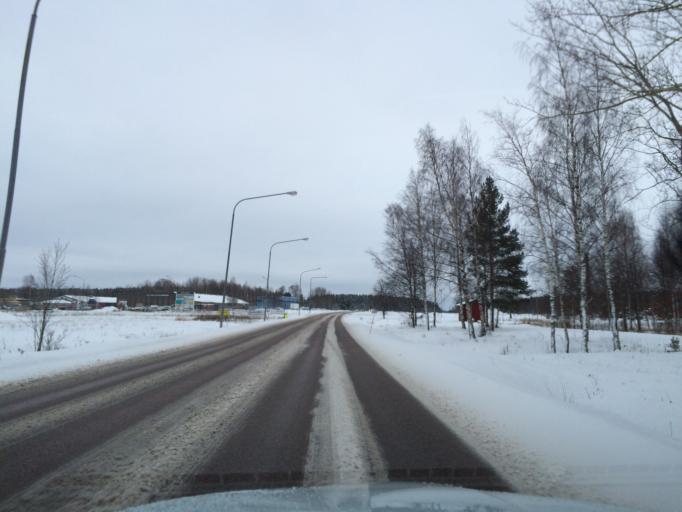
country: SE
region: Vaestmanland
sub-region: Hallstahammars Kommun
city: Hallstahammar
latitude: 59.6057
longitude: 16.2478
